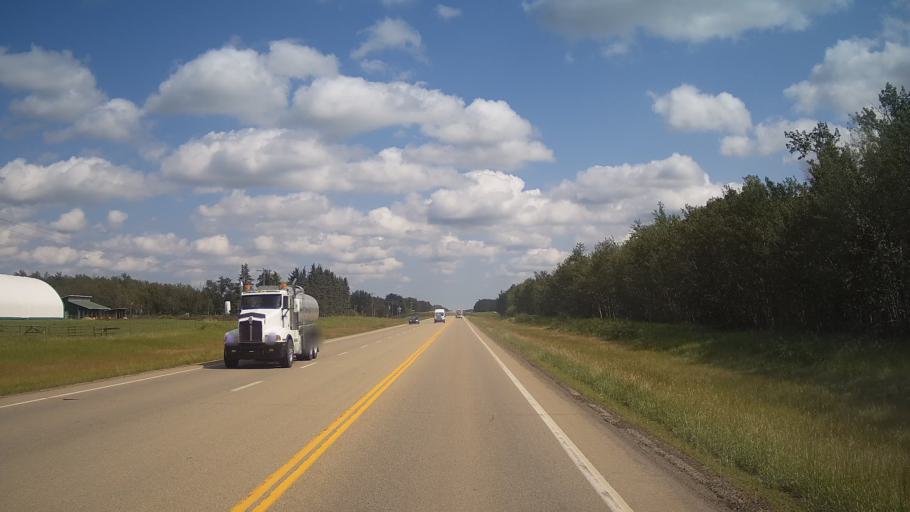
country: CA
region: Alberta
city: Sherwood Park
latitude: 53.3957
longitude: -113.0688
